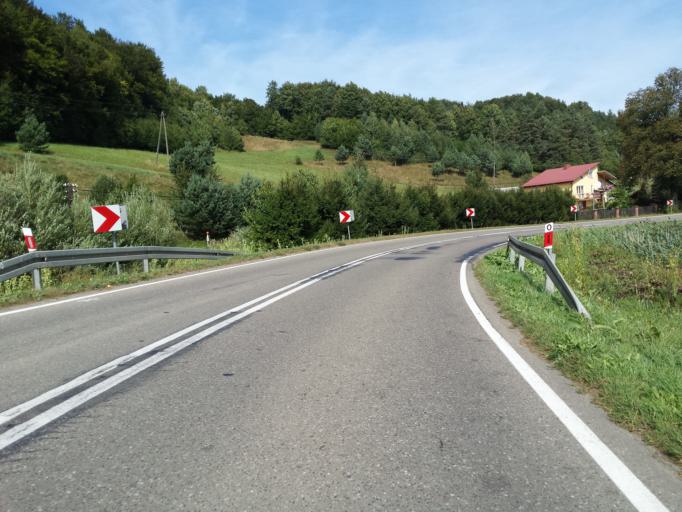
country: PL
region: Subcarpathian Voivodeship
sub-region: Powiat leski
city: Baligrod
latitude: 49.3966
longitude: 22.2794
